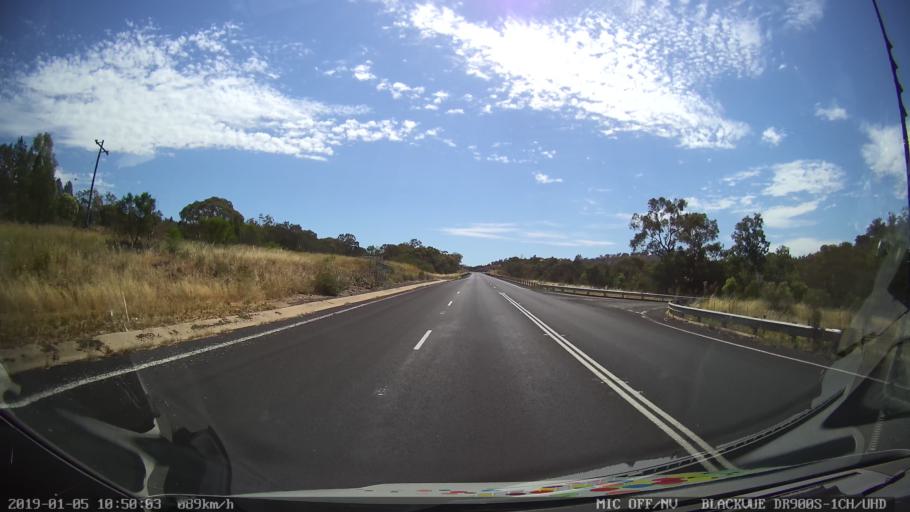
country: AU
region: New South Wales
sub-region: Warrumbungle Shire
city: Coonabarabran
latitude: -31.4303
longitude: 149.0697
